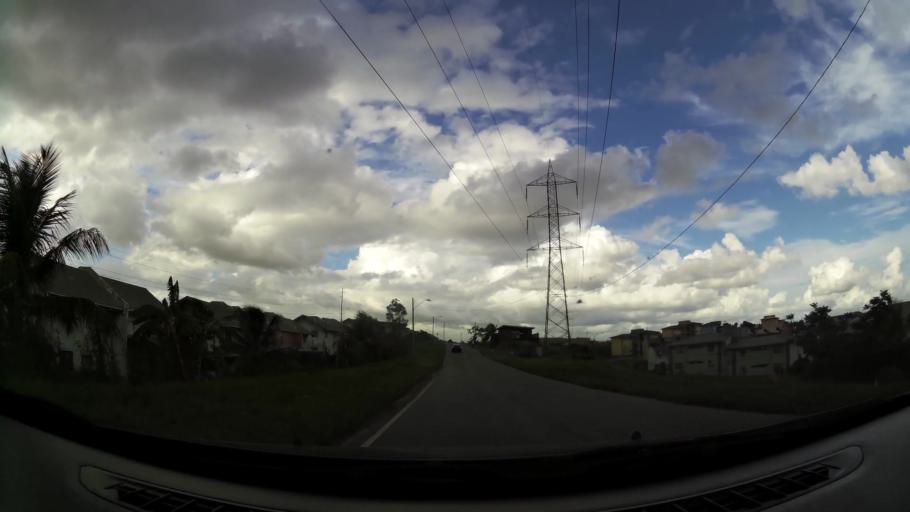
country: TT
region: City of San Fernando
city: Mon Repos
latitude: 10.2682
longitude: -61.4412
